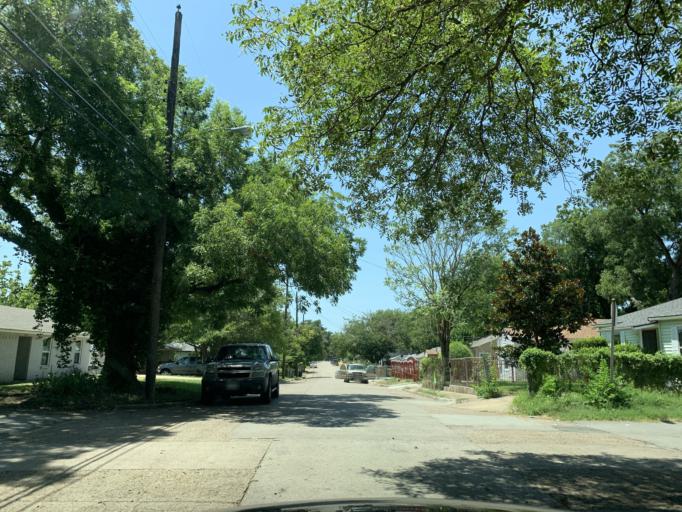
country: US
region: Texas
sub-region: Dallas County
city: Dallas
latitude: 32.6883
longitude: -96.8013
